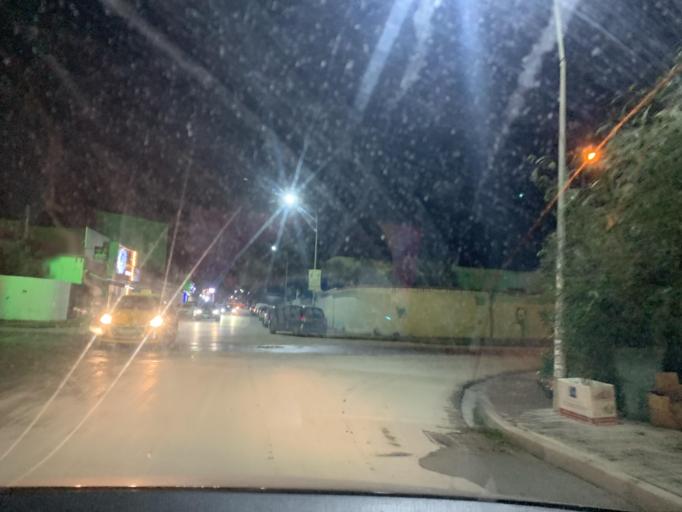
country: TN
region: Ariana
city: Ariana
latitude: 36.8549
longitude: 10.1754
